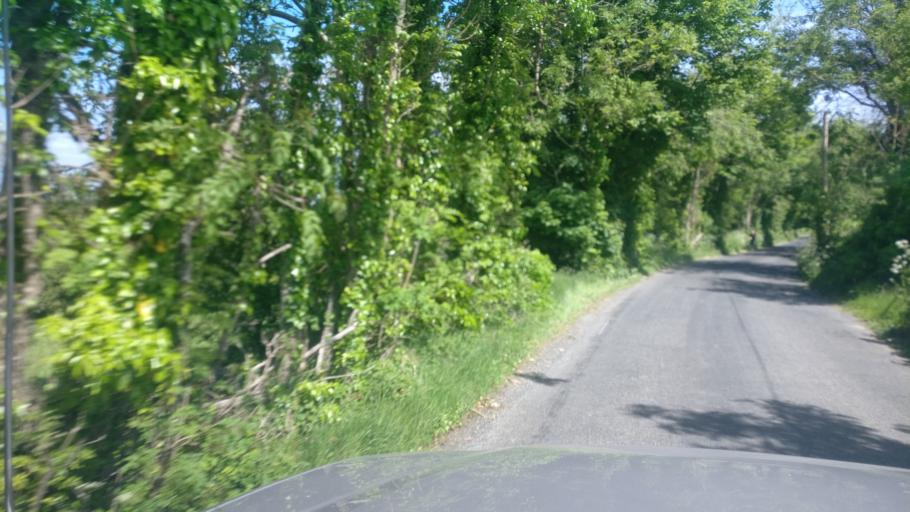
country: IE
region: Connaught
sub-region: County Galway
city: Gort
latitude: 53.1332
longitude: -8.7728
